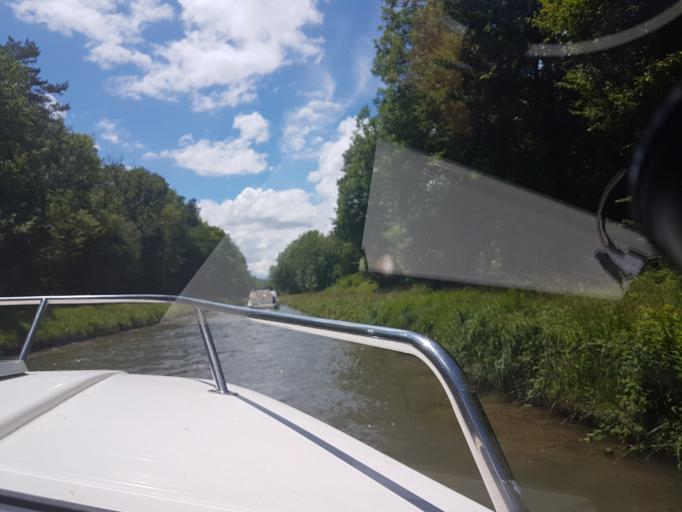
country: FR
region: Bourgogne
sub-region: Departement de l'Yonne
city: Vermenton
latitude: 47.5938
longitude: 3.6684
